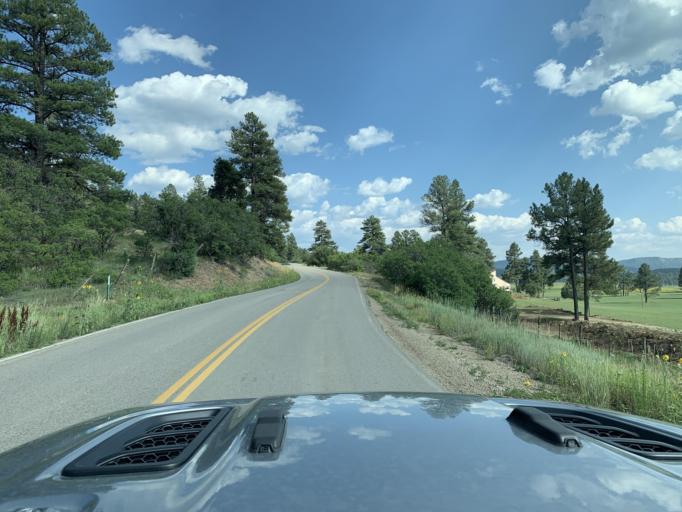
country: US
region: Colorado
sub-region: Archuleta County
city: Pagosa Springs
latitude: 37.2443
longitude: -107.0325
